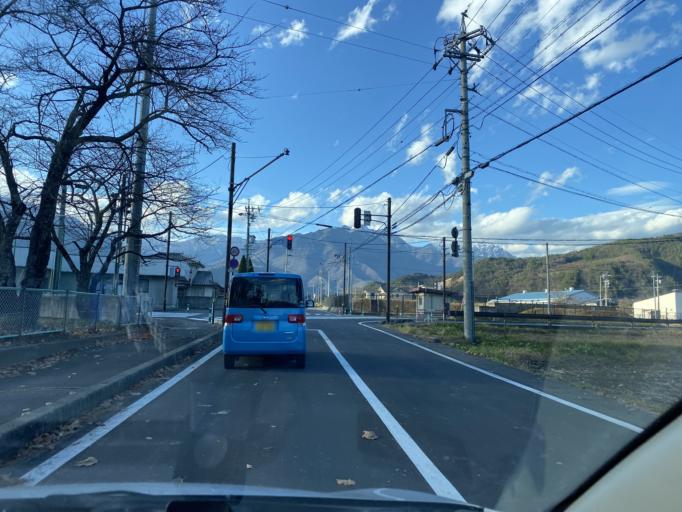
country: JP
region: Nagano
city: Omachi
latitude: 36.5224
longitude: 137.8339
